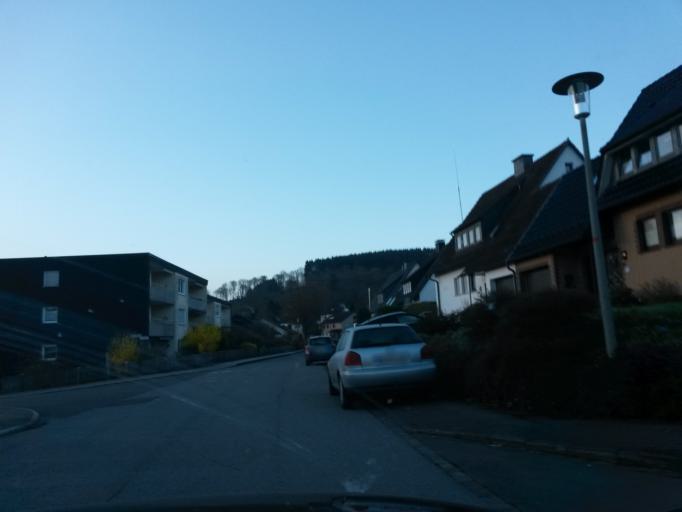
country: DE
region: North Rhine-Westphalia
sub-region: Regierungsbezirk Arnsberg
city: Herscheid
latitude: 51.1743
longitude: 7.7478
